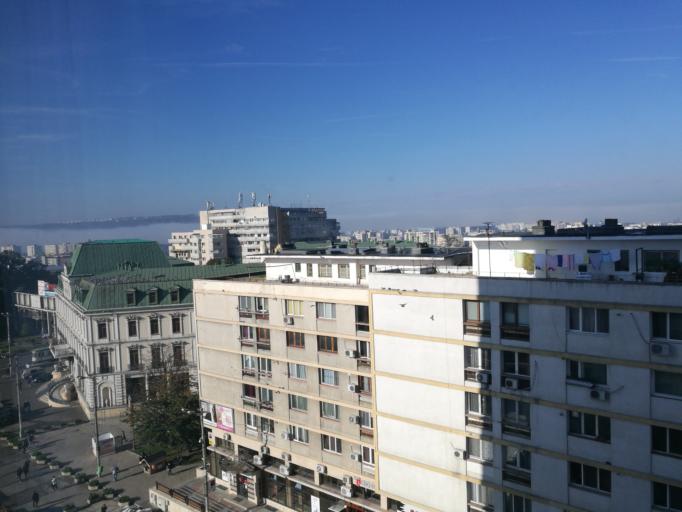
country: RO
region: Iasi
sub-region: Municipiul Iasi
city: Iasi
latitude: 47.1670
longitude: 27.5804
